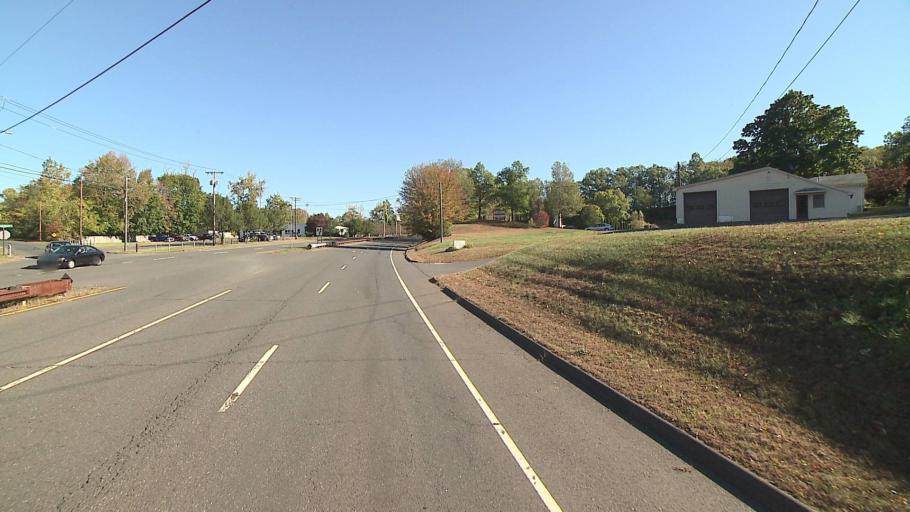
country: US
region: Connecticut
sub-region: Middlesex County
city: Portland
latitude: 41.5739
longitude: -72.6124
